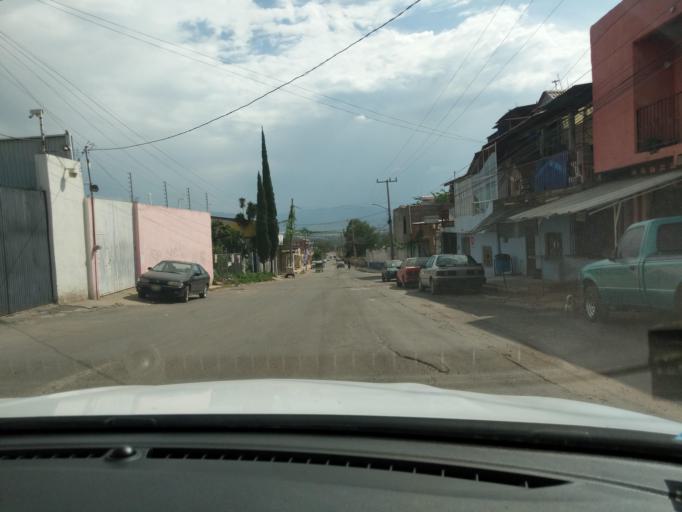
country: MX
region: Jalisco
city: San Jose del Castillo
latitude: 20.5187
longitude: -103.2350
